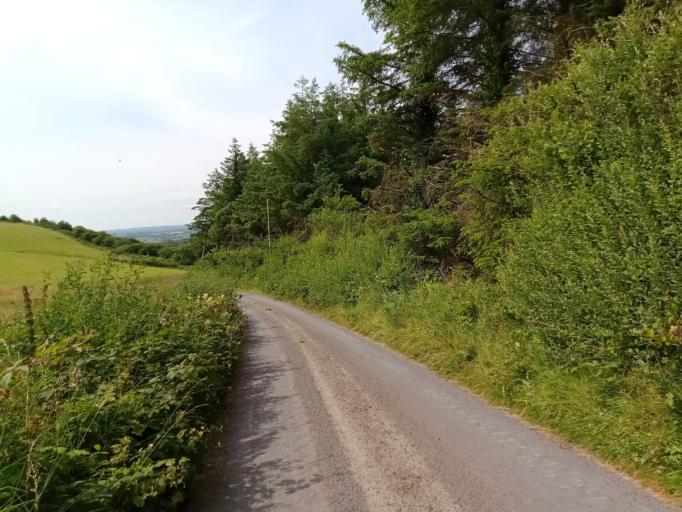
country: IE
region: Leinster
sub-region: Laois
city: Rathdowney
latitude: 52.7989
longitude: -7.4646
